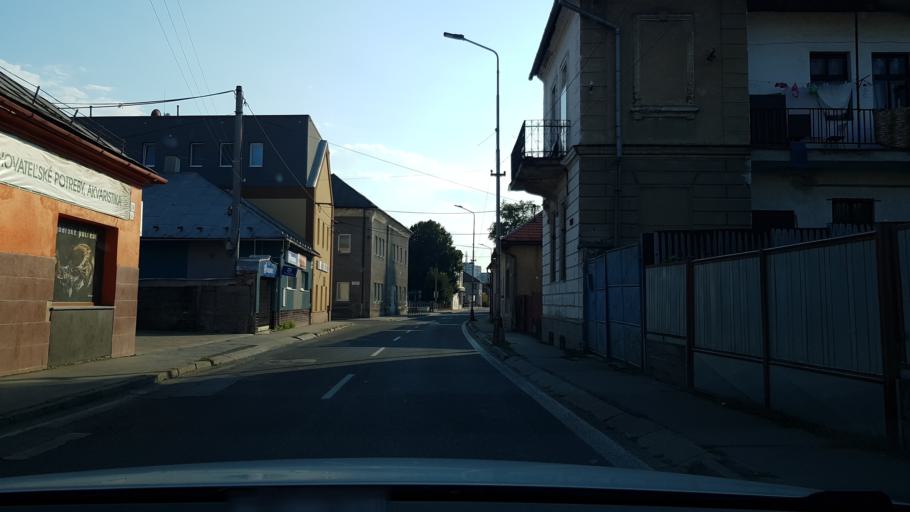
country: SK
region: Zilinsky
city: Bytca
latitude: 49.2232
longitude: 18.5612
